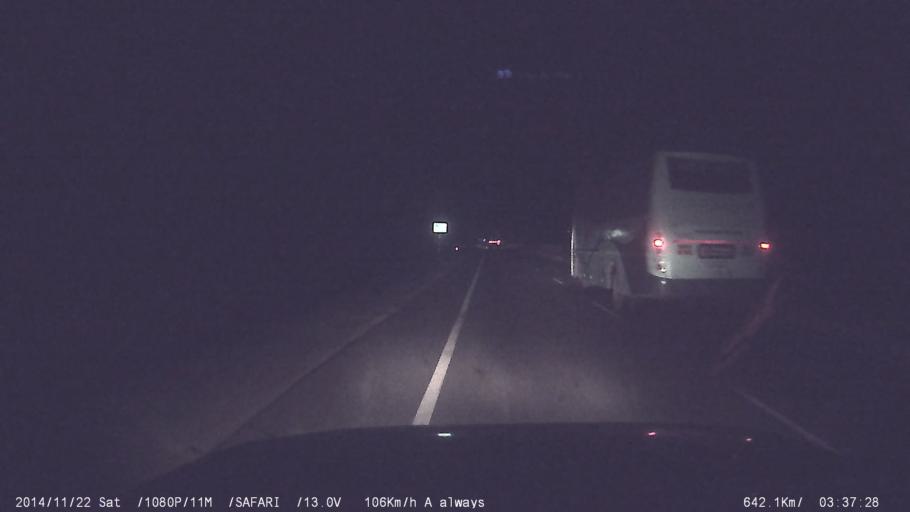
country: IN
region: Tamil Nadu
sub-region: Salem
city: Idappadi
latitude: 11.4845
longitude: 77.8443
